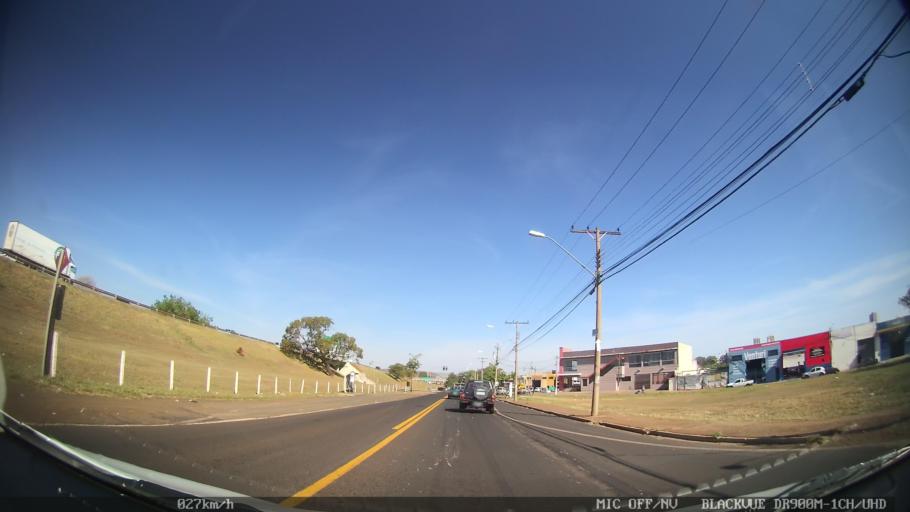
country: BR
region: Sao Paulo
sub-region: Ribeirao Preto
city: Ribeirao Preto
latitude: -21.1869
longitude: -47.7578
